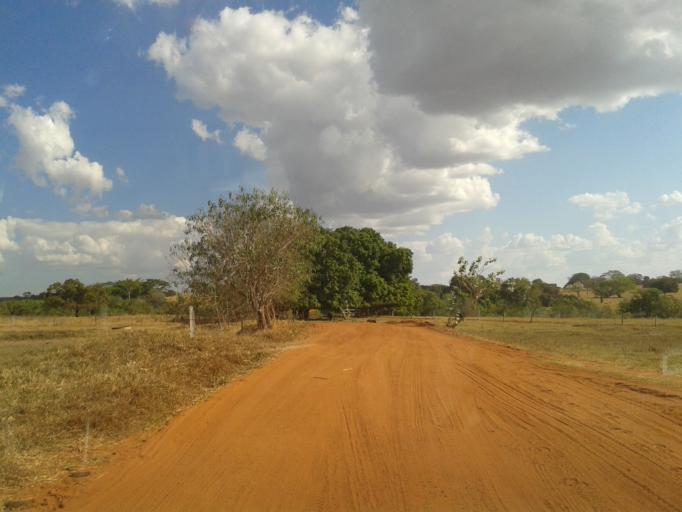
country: BR
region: Minas Gerais
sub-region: Santa Vitoria
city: Santa Vitoria
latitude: -19.2702
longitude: -49.9905
